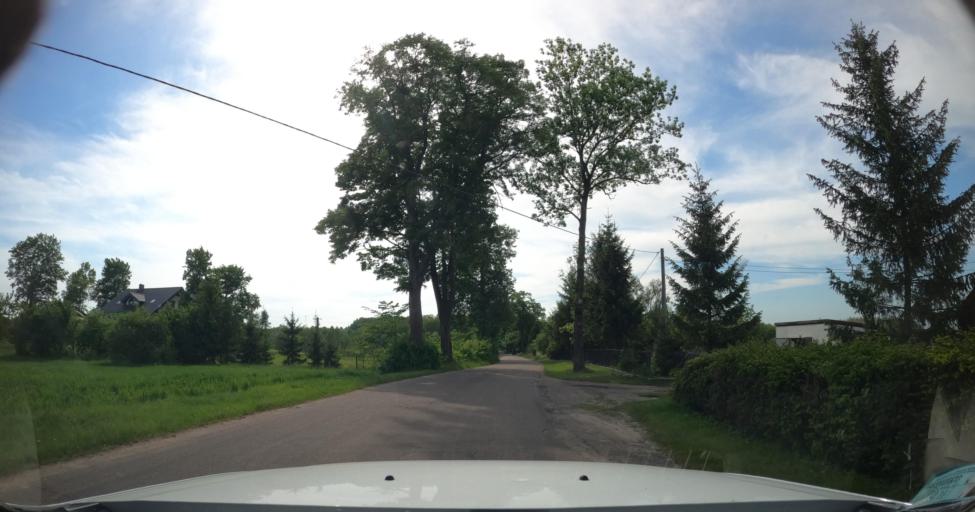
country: PL
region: Warmian-Masurian Voivodeship
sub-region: Powiat ostrodzki
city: Milakowo
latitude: 54.0102
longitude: 20.1062
